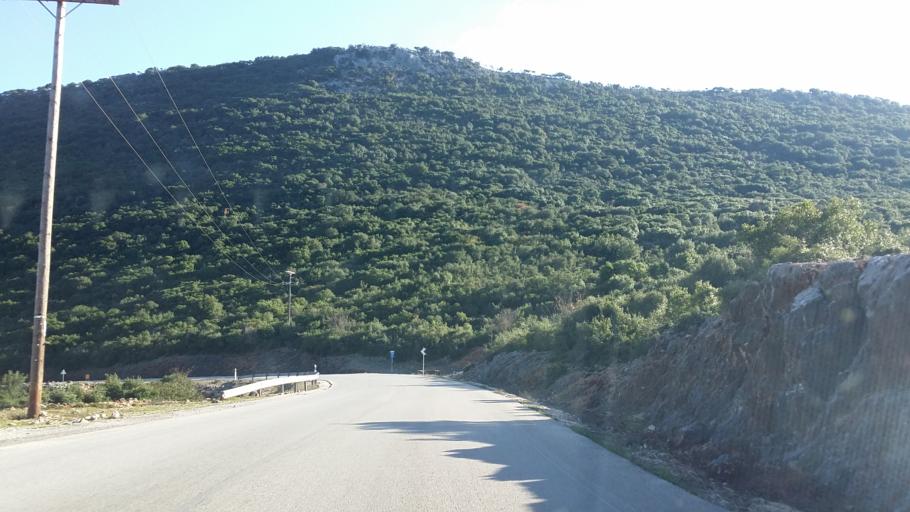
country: GR
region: West Greece
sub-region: Nomos Aitolias kai Akarnanias
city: Astakos
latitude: 38.6086
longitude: 21.1274
